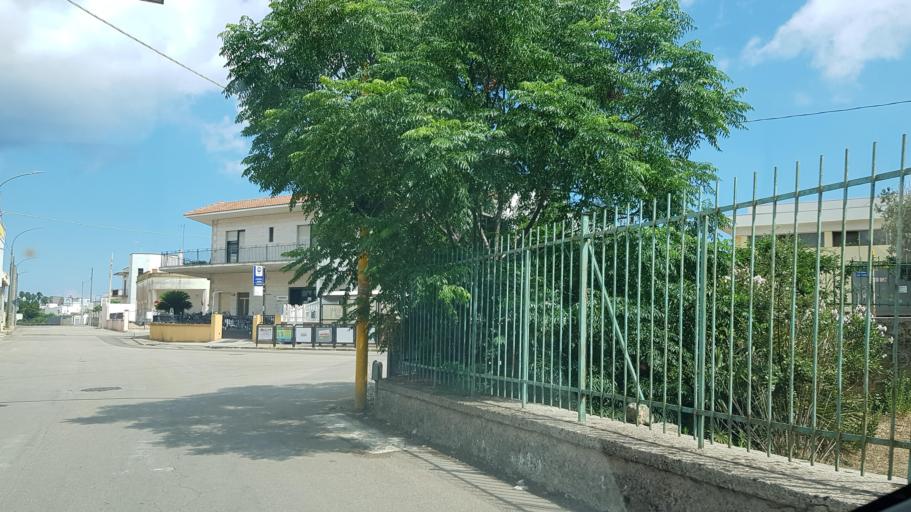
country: IT
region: Apulia
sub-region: Provincia di Lecce
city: Castrignano del Capo
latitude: 39.8345
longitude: 18.3517
